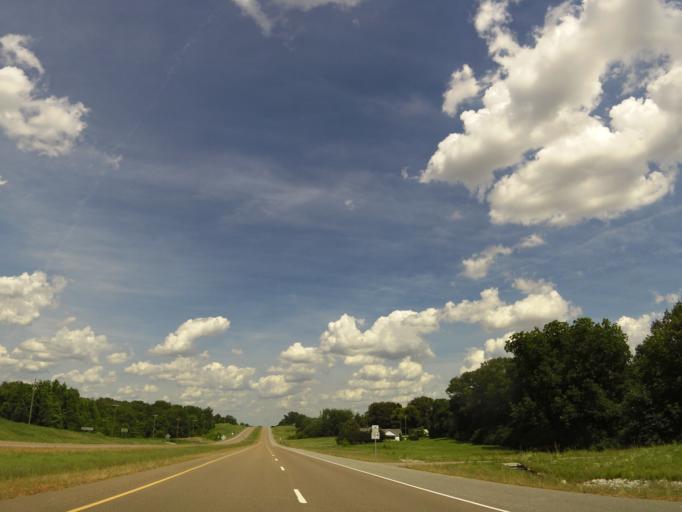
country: US
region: Tennessee
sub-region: Gibson County
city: Dyer
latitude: 35.9947
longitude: -89.1163
